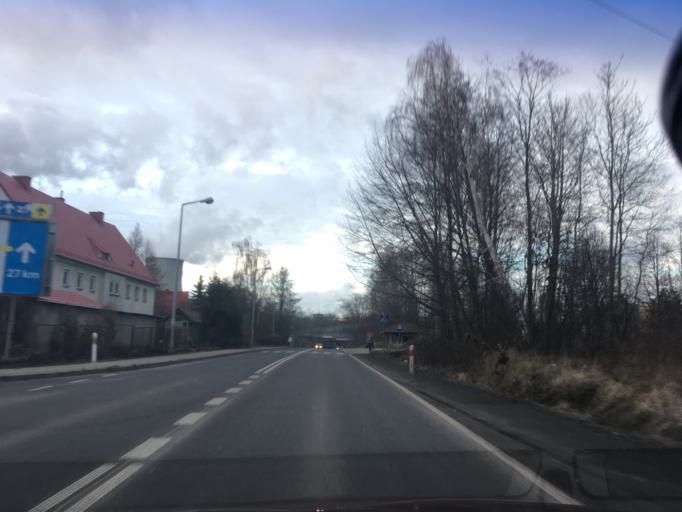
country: DE
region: Saxony
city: Hirschfelde
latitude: 50.9420
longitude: 14.9205
